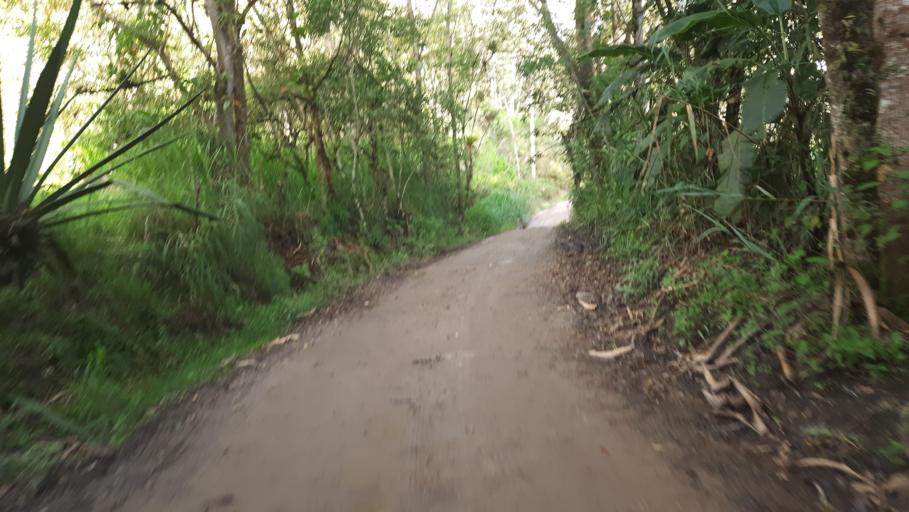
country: CO
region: Cundinamarca
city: Tenza
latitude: 5.1031
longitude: -73.4304
